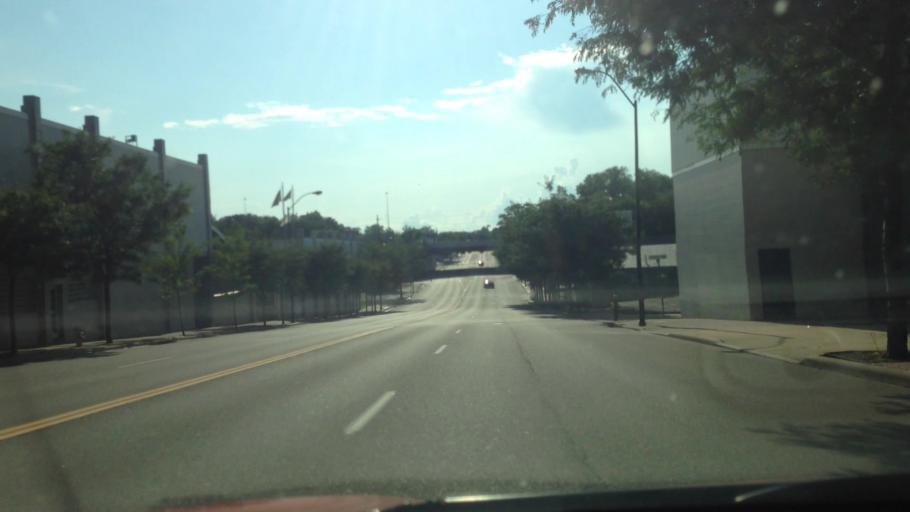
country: US
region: Ohio
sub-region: Summit County
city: Akron
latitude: 41.0712
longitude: -81.5009
